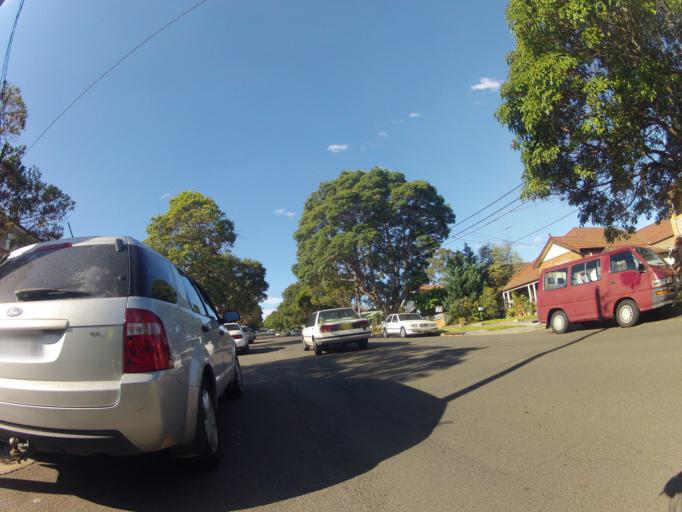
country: AU
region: New South Wales
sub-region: Hurstville
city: Penshurst
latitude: -33.9683
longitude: 151.0797
